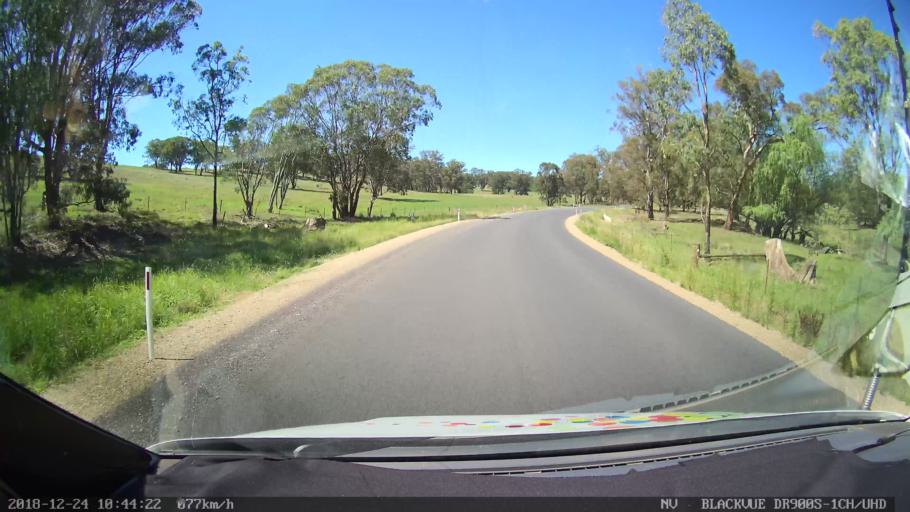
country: AU
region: New South Wales
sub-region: Upper Hunter Shire
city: Merriwa
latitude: -31.8923
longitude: 150.4440
